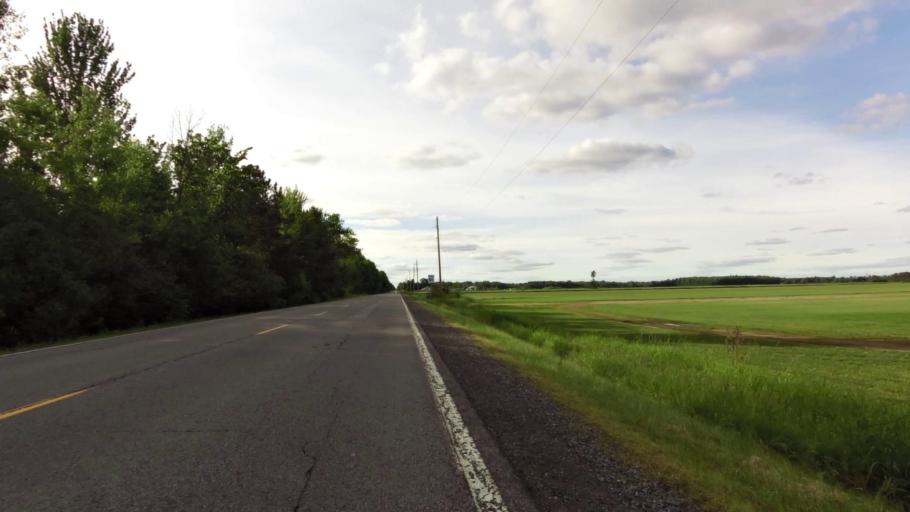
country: CA
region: Ontario
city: Ottawa
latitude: 45.1907
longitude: -75.5860
